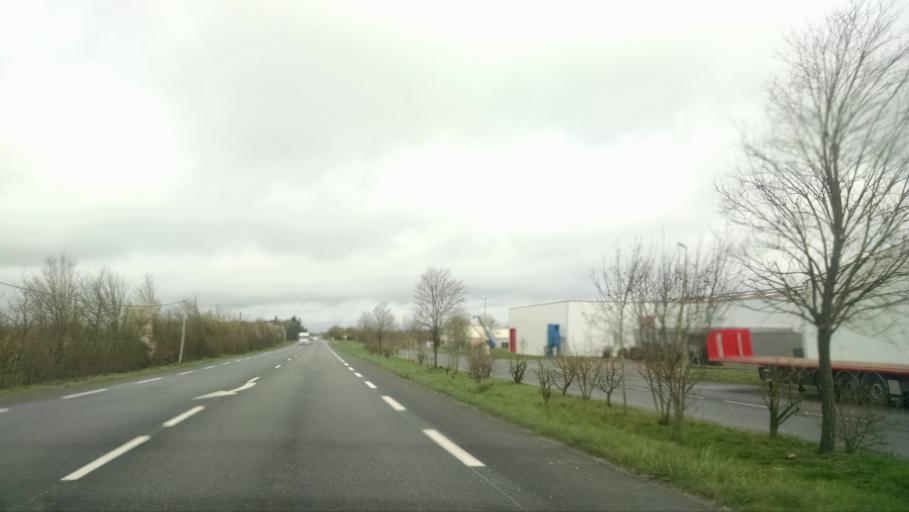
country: FR
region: Pays de la Loire
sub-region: Departement de la Vendee
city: Saint-Hilaire-de-Loulay
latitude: 47.0247
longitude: -1.3484
